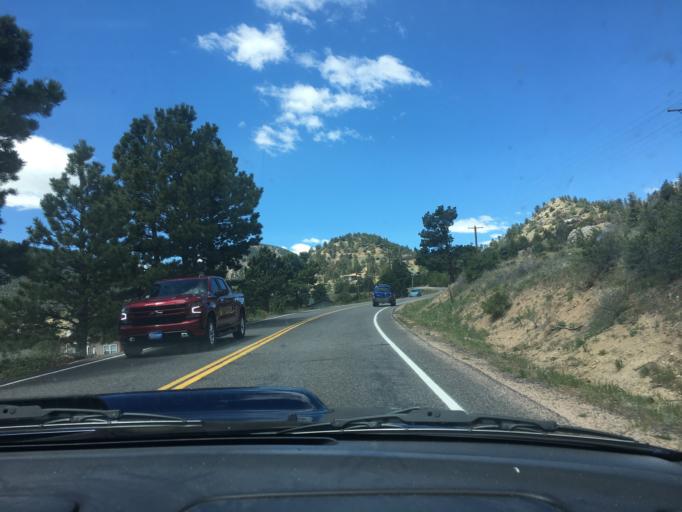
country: US
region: Colorado
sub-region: Larimer County
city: Estes Park
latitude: 40.3531
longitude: -105.5209
